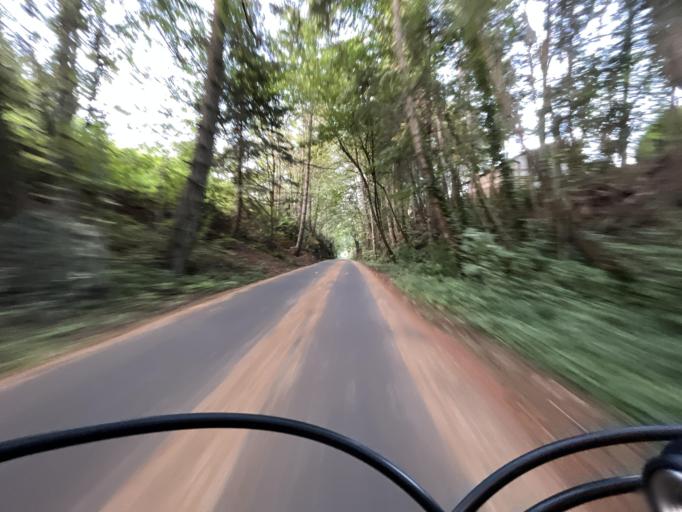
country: CA
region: British Columbia
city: Colwood
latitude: 48.4587
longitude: -123.4617
